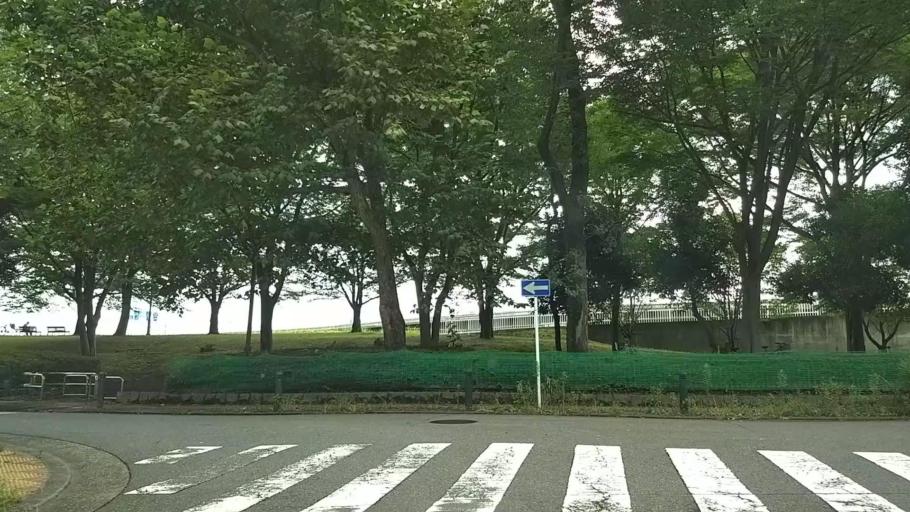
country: JP
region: Kanagawa
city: Yokohama
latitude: 35.5119
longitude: 139.6165
